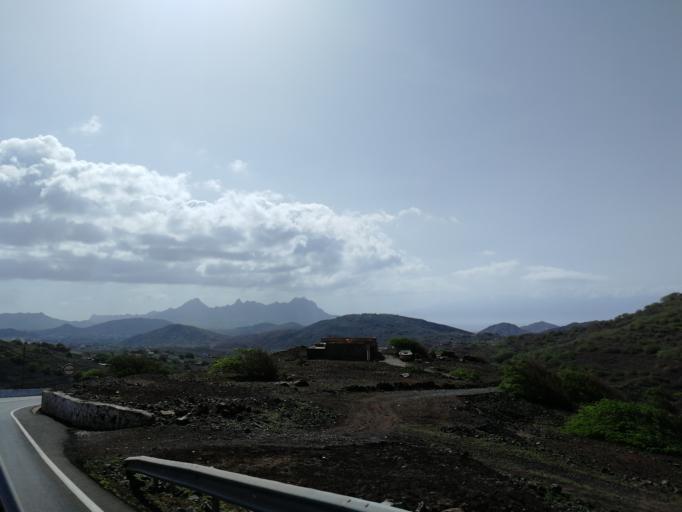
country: CV
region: Sao Vicente
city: Mindelo
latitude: 16.8753
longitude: -24.9494
